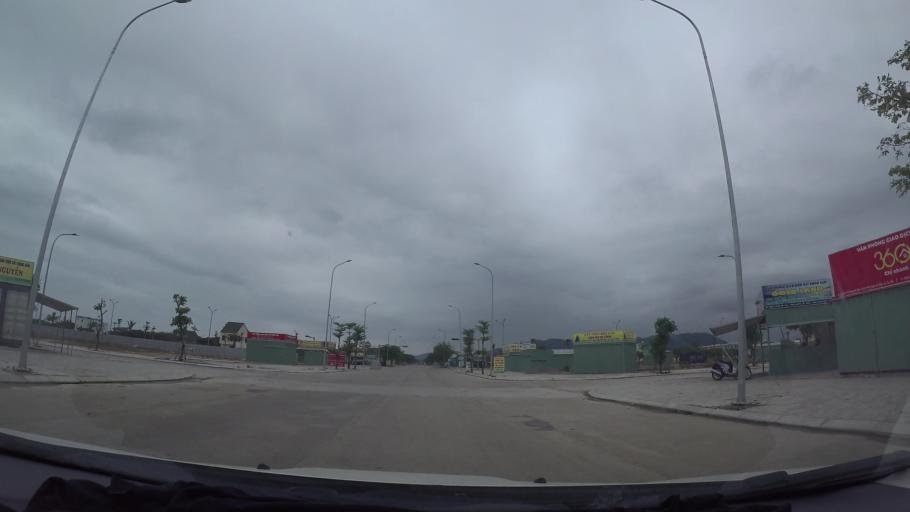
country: VN
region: Da Nang
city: Lien Chieu
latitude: 16.1062
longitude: 108.1172
